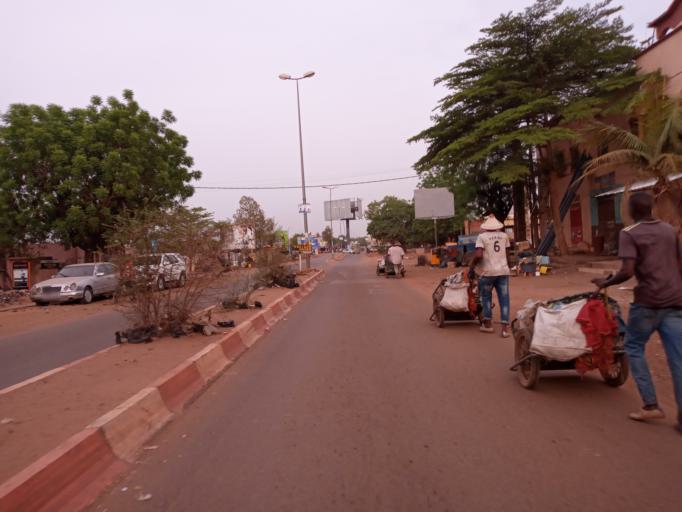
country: ML
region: Bamako
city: Bamako
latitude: 12.6620
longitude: -7.9768
